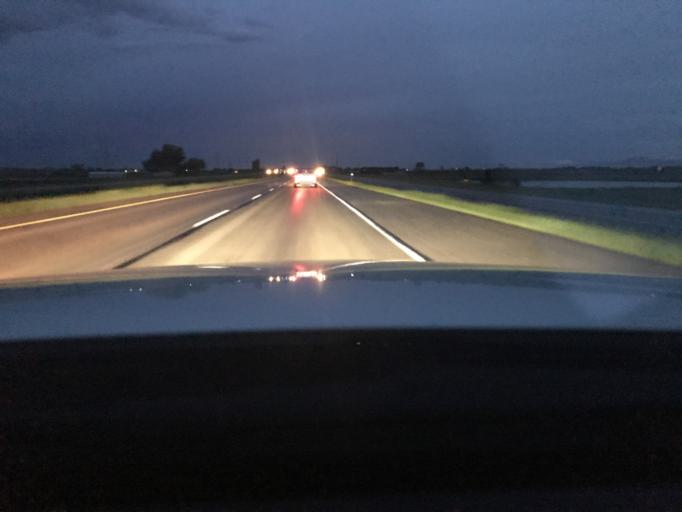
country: US
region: Colorado
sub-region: Larimer County
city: Wellington
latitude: 40.6790
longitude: -105.0011
